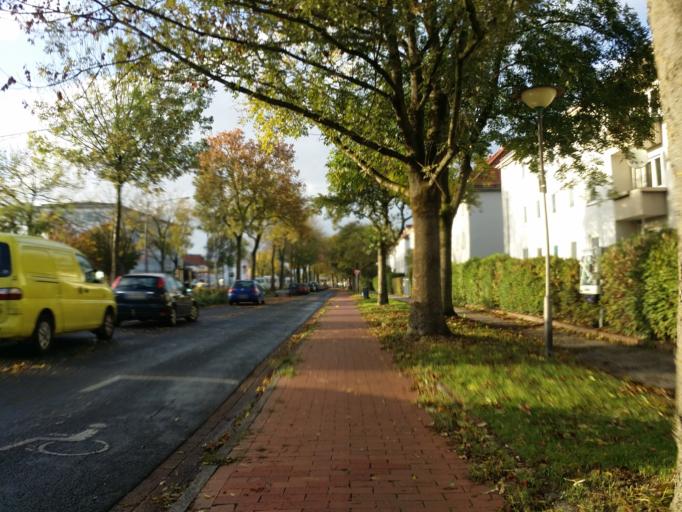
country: DE
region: Bremen
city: Bremen
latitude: 53.0648
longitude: 8.7857
